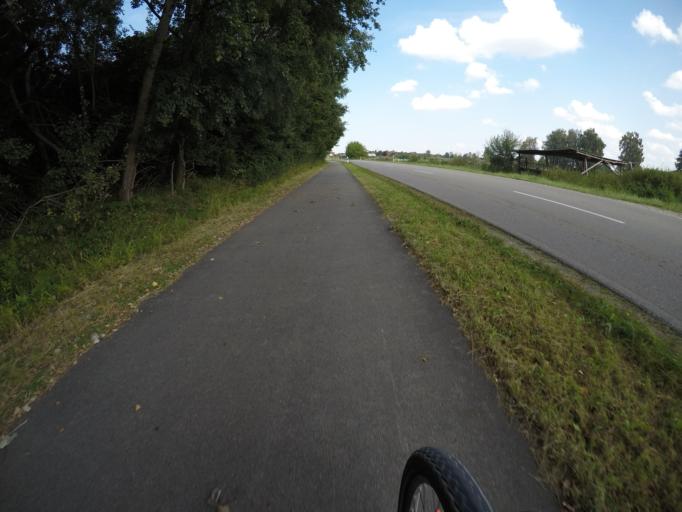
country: DE
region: Bavaria
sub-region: Swabia
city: Kuhlenthal
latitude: 48.5555
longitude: 10.8190
